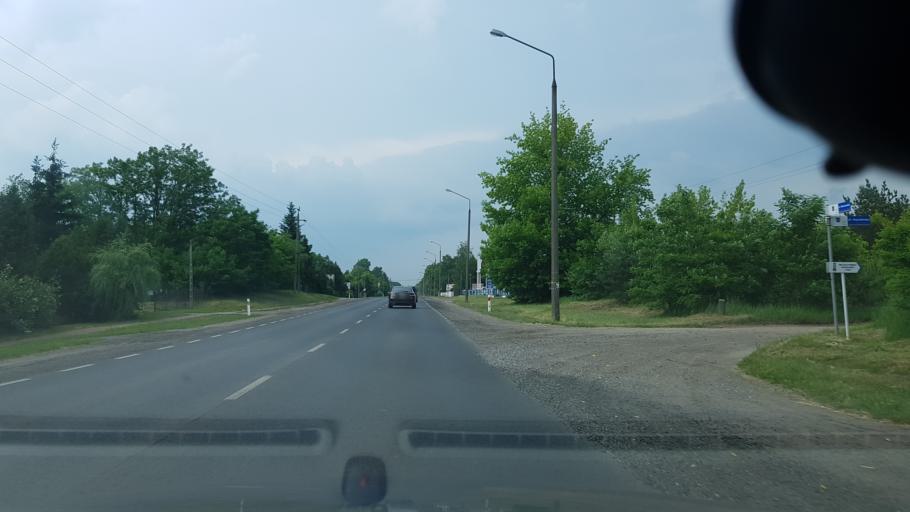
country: PL
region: Masovian Voivodeship
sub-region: Powiat legionowski
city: Michalow-Reginow
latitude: 52.4239
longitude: 20.9748
